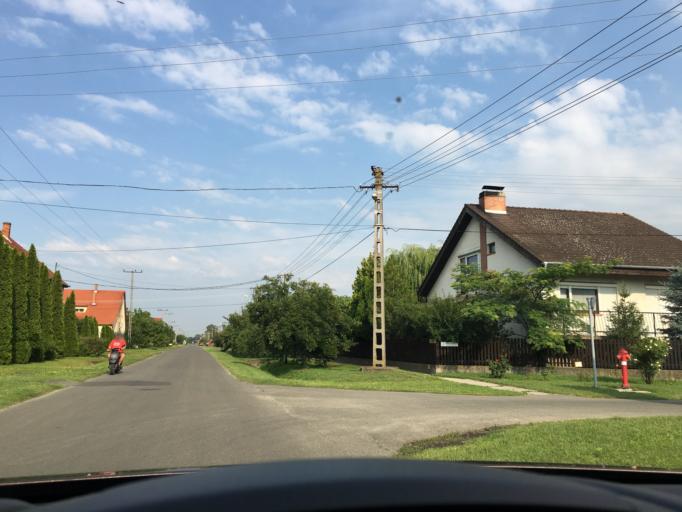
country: HU
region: Csongrad
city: Morahalom
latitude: 46.2101
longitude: 19.8860
